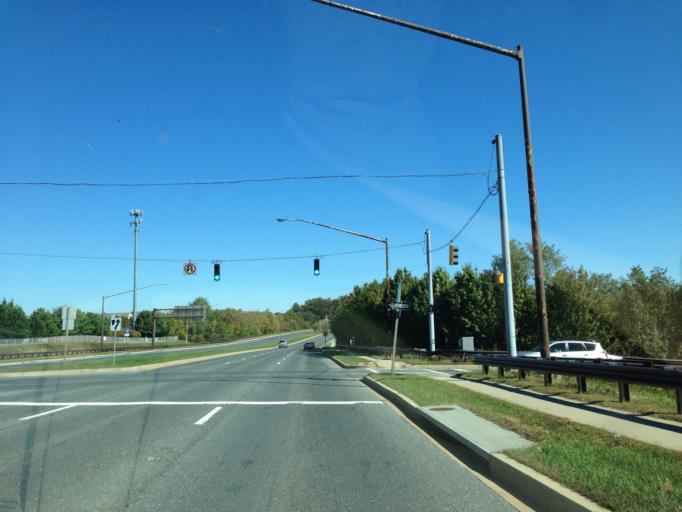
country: US
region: Maryland
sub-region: Montgomery County
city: Germantown
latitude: 39.1986
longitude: -77.2612
